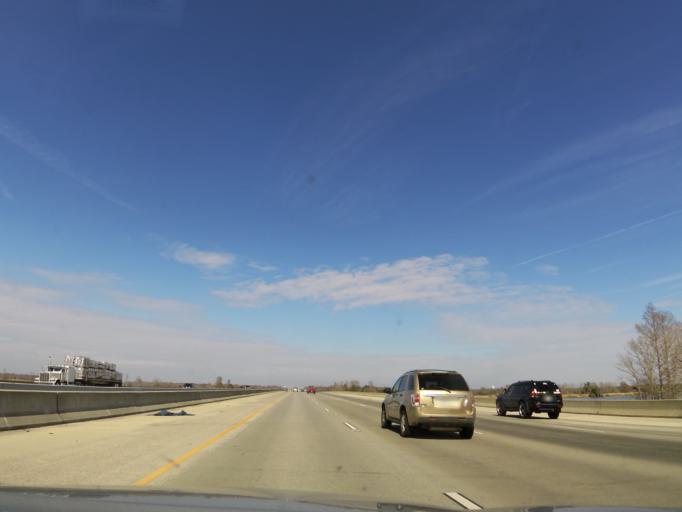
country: US
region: Georgia
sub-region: McIntosh County
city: Darien
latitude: 31.3508
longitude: -81.4612
